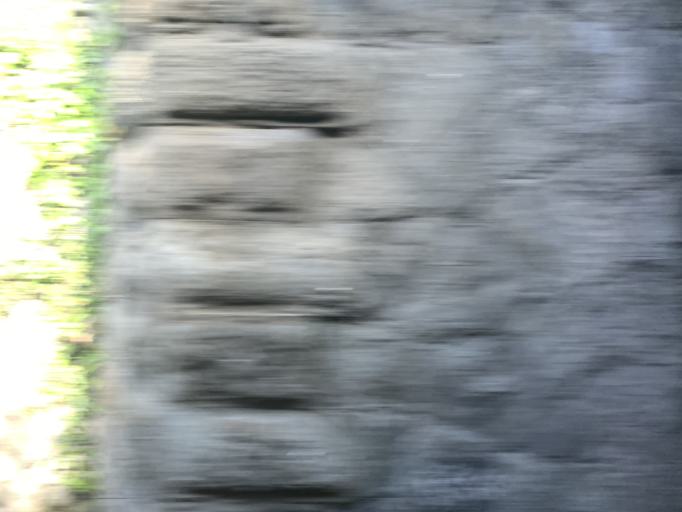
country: IT
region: Latium
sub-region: Citta metropolitana di Roma Capitale
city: Marino
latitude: 41.7782
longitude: 12.6403
